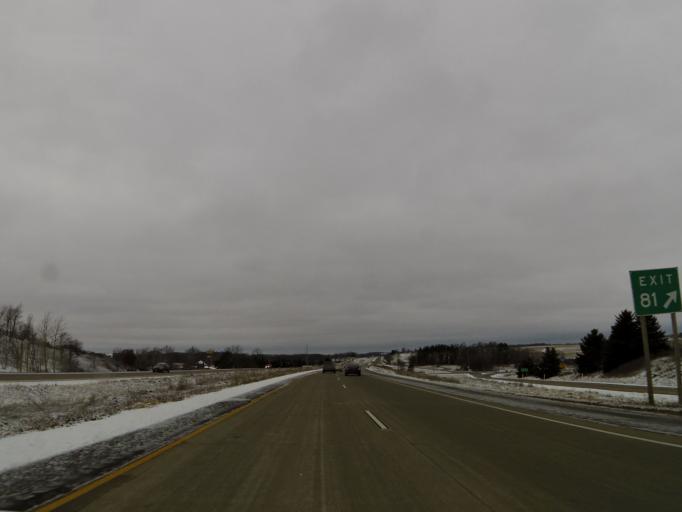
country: US
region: Wisconsin
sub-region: Trempealeau County
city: Osseo
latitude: 44.6403
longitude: -91.3044
